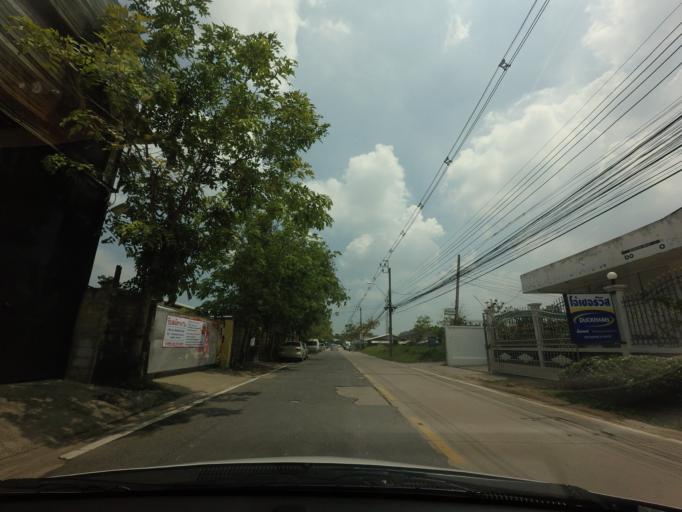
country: TH
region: Bangkok
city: Taling Chan
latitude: 13.7768
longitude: 100.4166
